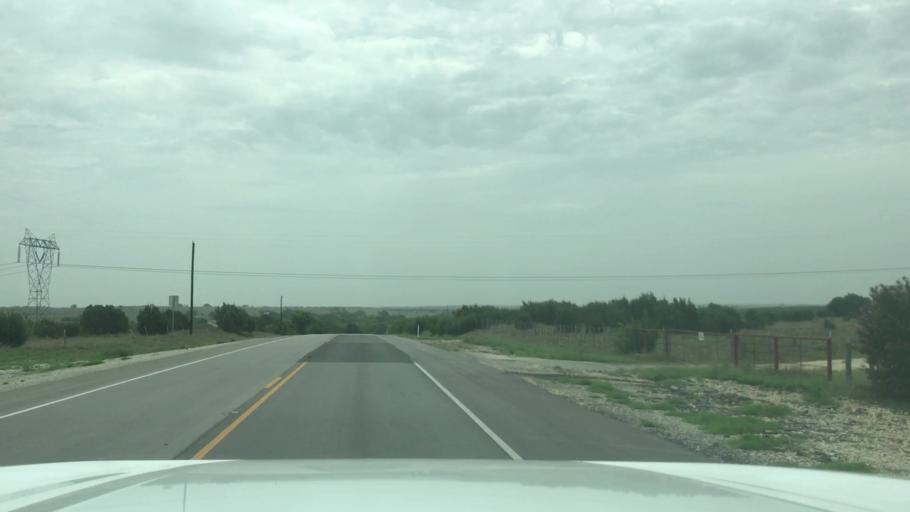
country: US
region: Texas
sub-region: Erath County
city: Dublin
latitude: 32.0770
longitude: -98.2372
